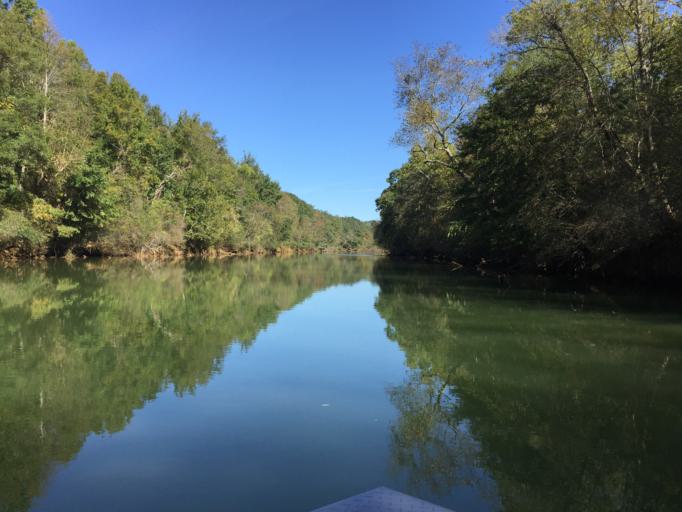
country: US
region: Georgia
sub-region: Fulton County
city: Johns Creek
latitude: 34.0173
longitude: -84.1761
